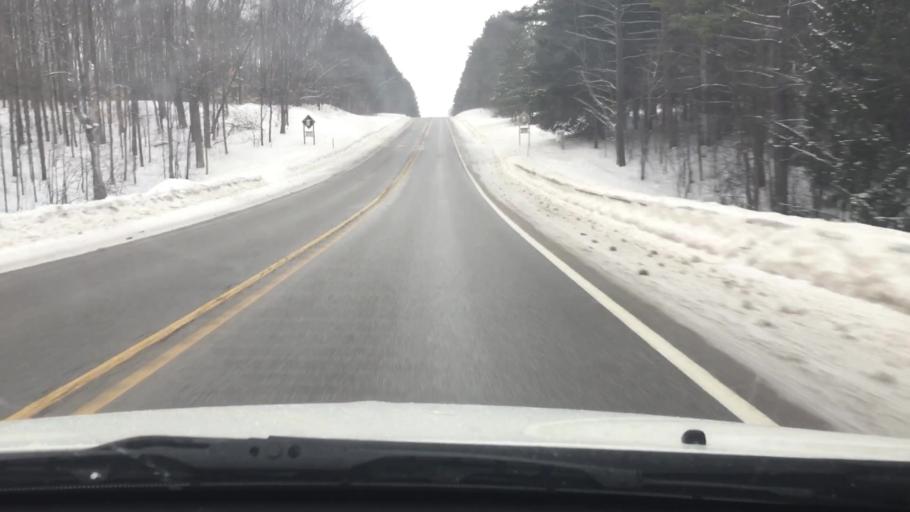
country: US
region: Michigan
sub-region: Otsego County
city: Gaylord
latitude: 45.0617
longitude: -84.8039
